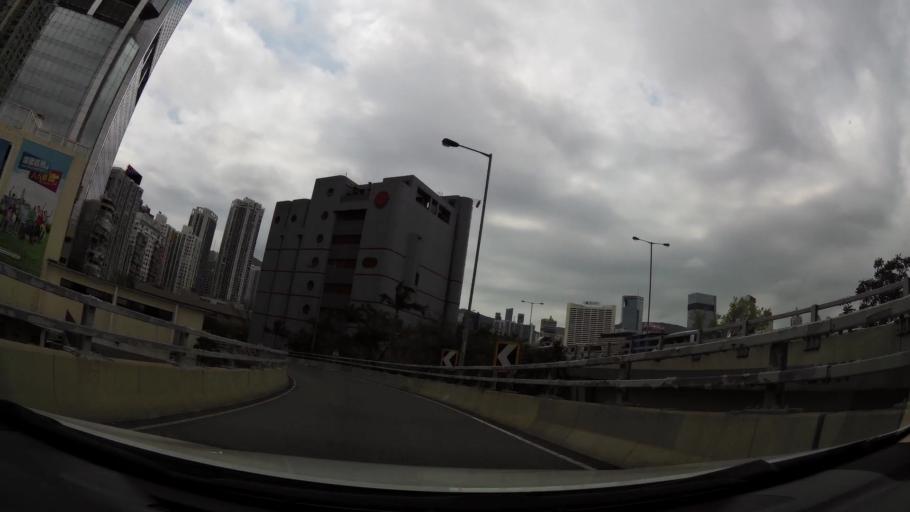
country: HK
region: Wanchai
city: Wan Chai
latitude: 22.2868
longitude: 114.1895
